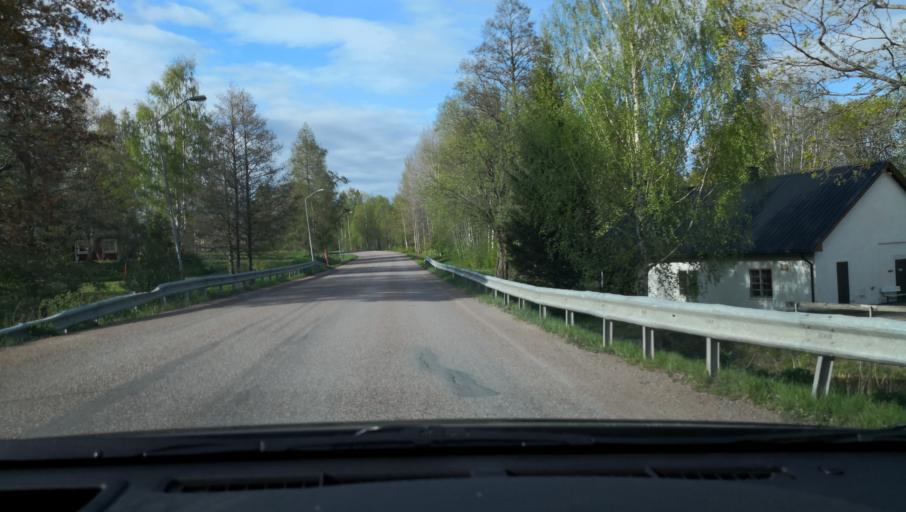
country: SE
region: Dalarna
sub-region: Saters Kommun
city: Saeter
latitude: 60.2933
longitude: 15.8260
